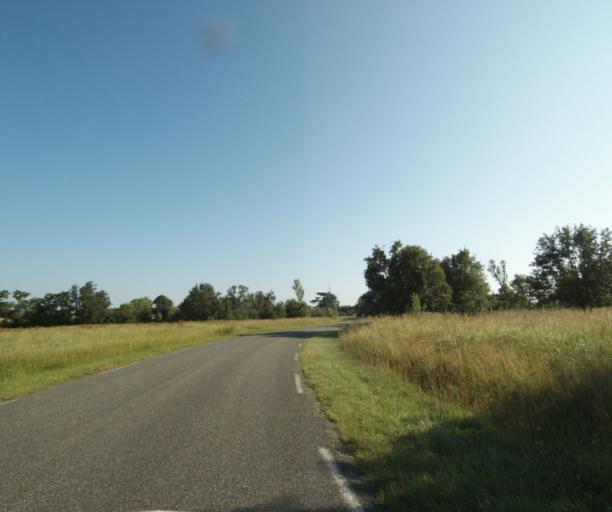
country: FR
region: Midi-Pyrenees
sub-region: Departement du Tarn-et-Garonne
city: Saint-Etienne-de-Tulmont
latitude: 44.0373
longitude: 1.4222
